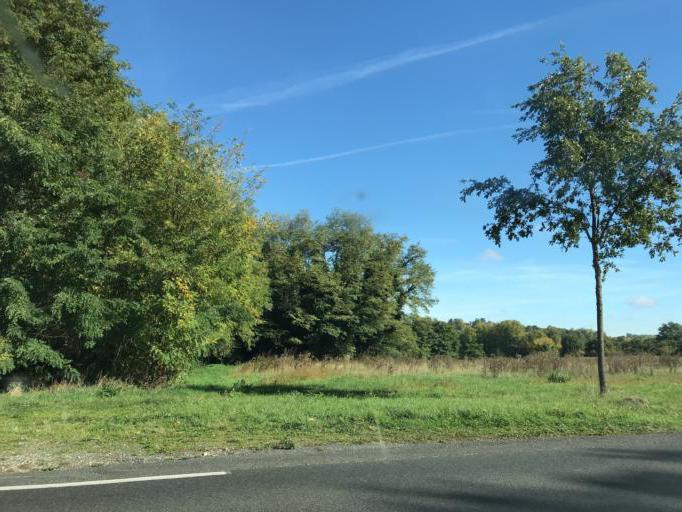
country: FR
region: Rhone-Alpes
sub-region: Departement de l'Ain
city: Guereins
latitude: 46.0997
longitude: 4.7765
